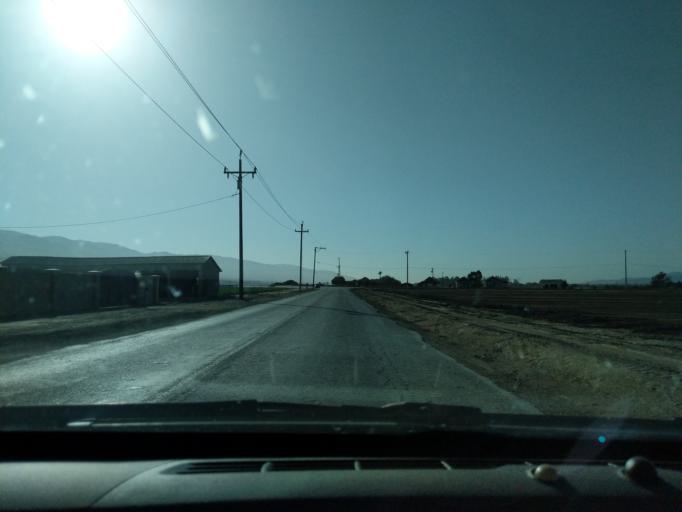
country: US
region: California
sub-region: Monterey County
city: Soledad
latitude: 36.4026
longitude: -121.3437
